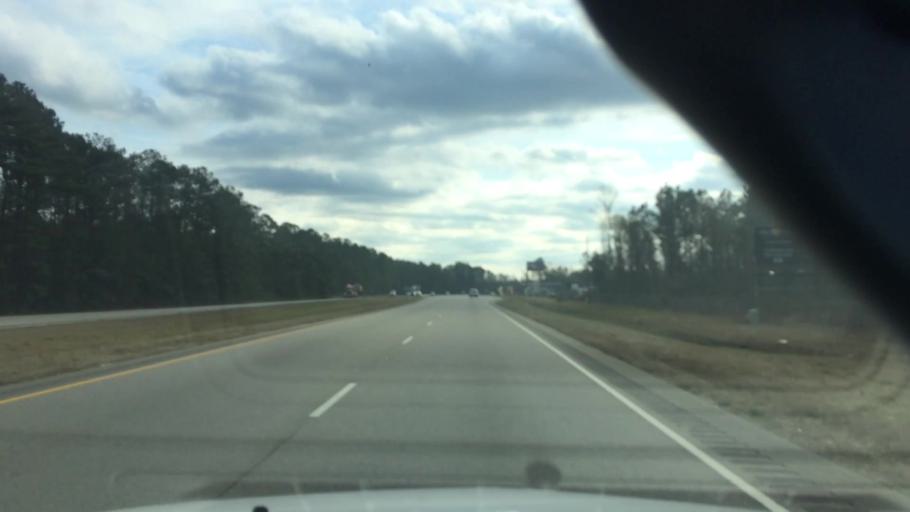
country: US
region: North Carolina
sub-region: Brunswick County
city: Bolivia
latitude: 34.1441
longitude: -78.0939
